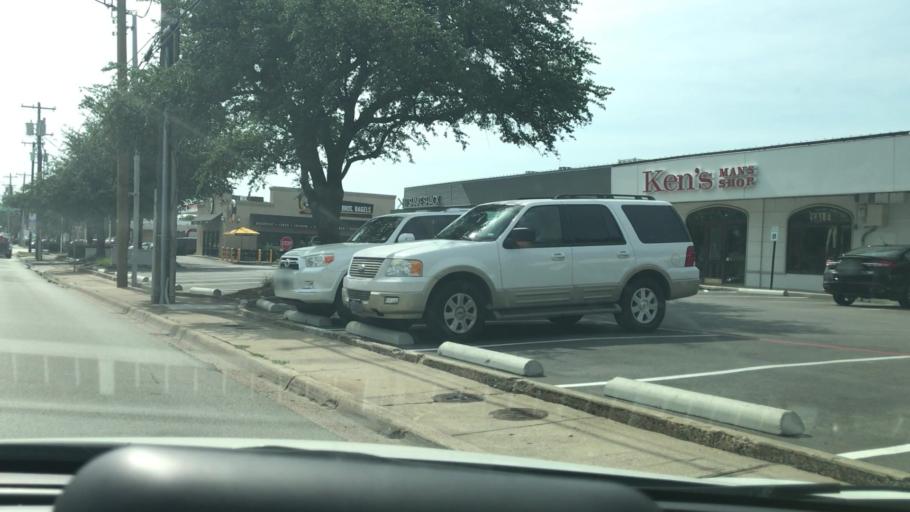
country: US
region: Texas
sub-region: Dallas County
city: University Park
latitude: 32.8949
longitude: -96.8025
